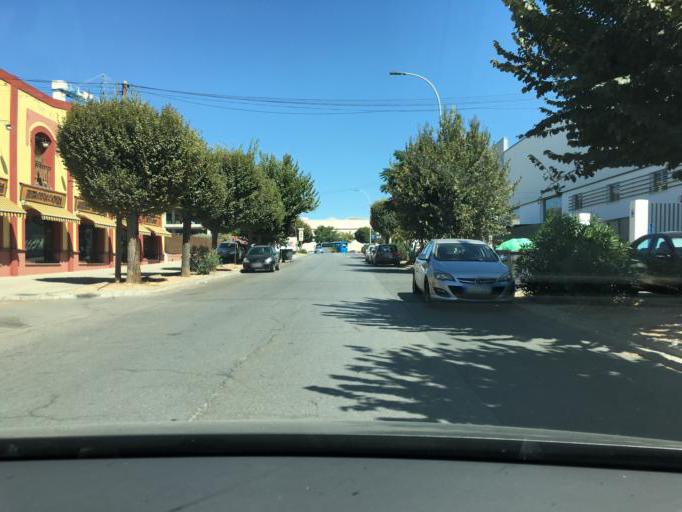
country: ES
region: Andalusia
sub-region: Provincia de Granada
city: Albolote
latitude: 37.2291
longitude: -3.6469
